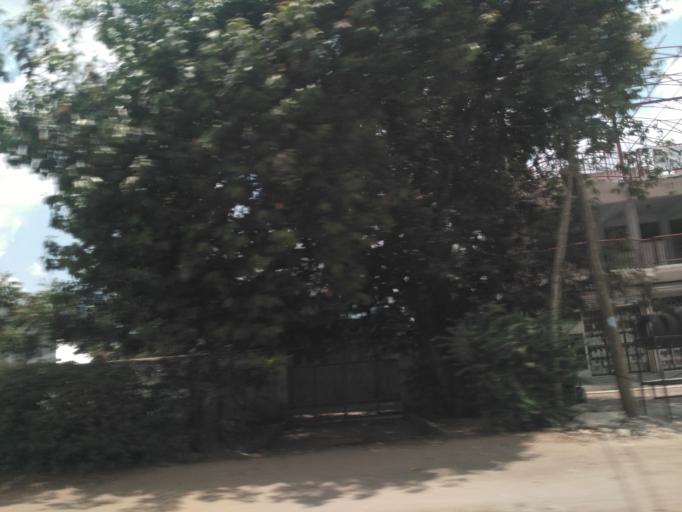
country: TZ
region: Dar es Salaam
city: Dar es Salaam
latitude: -6.8450
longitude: 39.3532
